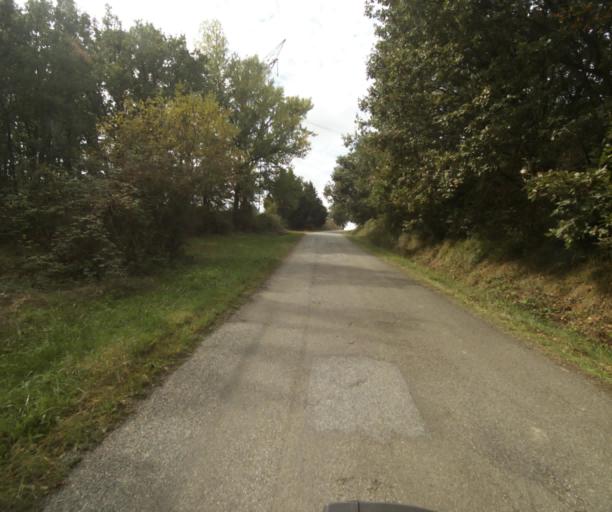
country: FR
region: Midi-Pyrenees
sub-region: Departement du Tarn-et-Garonne
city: Verdun-sur-Garonne
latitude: 43.8625
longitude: 1.1919
